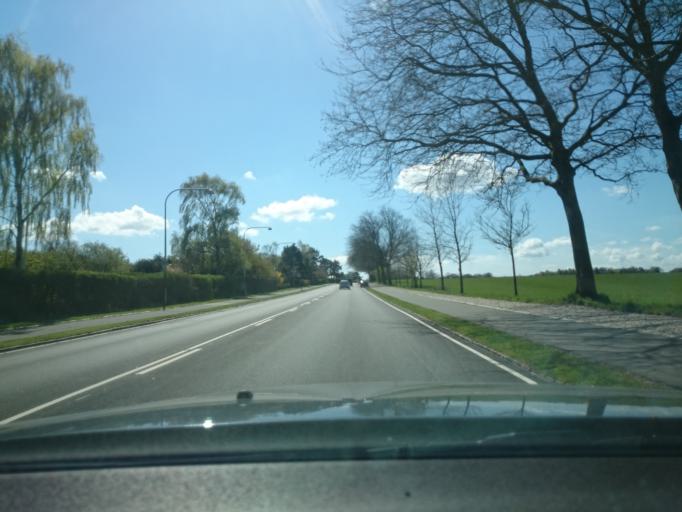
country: DK
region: Capital Region
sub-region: Lyngby-Tarbaek Kommune
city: Kongens Lyngby
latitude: 55.7860
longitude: 12.5417
